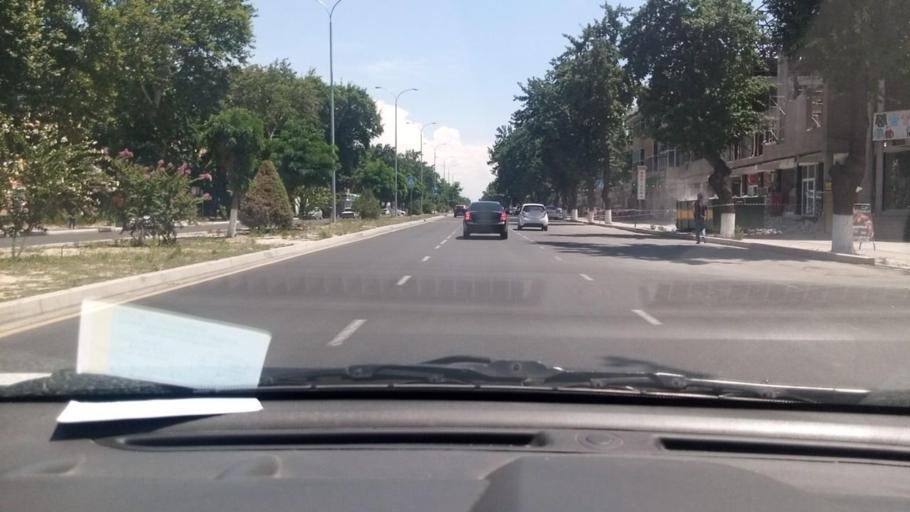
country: UZ
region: Toshkent Shahri
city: Tashkent
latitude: 41.2879
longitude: 69.2033
